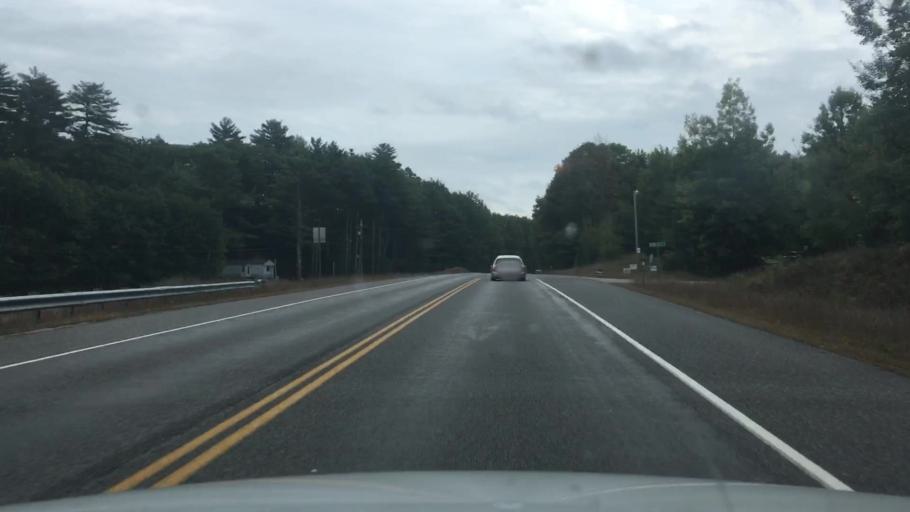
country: US
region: New Hampshire
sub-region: Strafford County
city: New Durham
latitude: 43.4943
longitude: -71.2566
